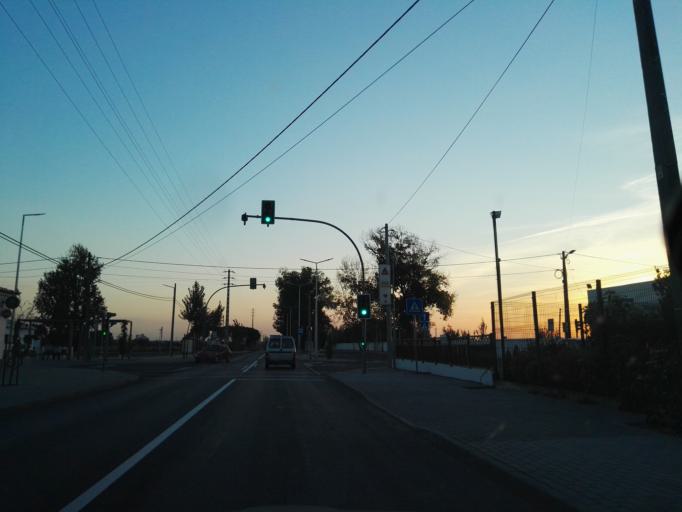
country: PT
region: Santarem
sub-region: Coruche
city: Coruche
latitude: 38.9546
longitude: -8.4930
